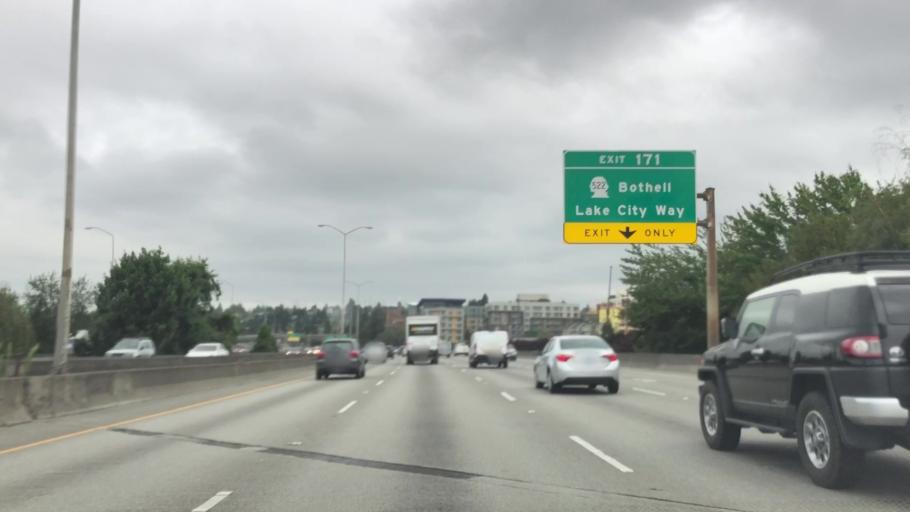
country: US
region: Washington
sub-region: King County
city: Seattle
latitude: 47.6735
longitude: -122.3224
